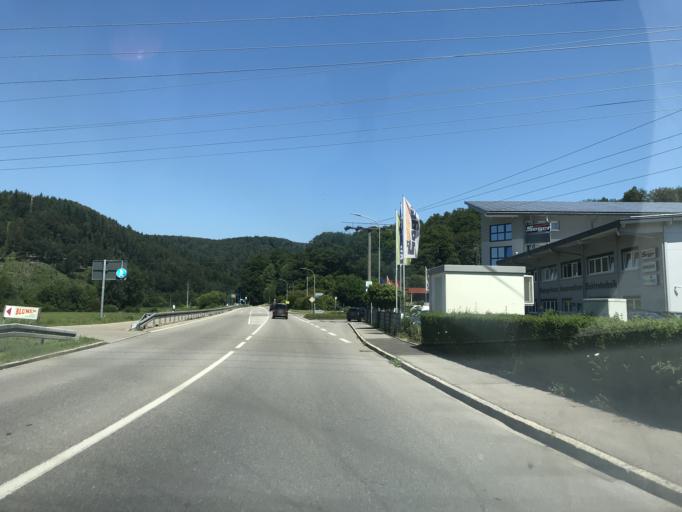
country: DE
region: Baden-Wuerttemberg
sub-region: Freiburg Region
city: Maulburg
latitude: 47.6493
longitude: 7.8004
